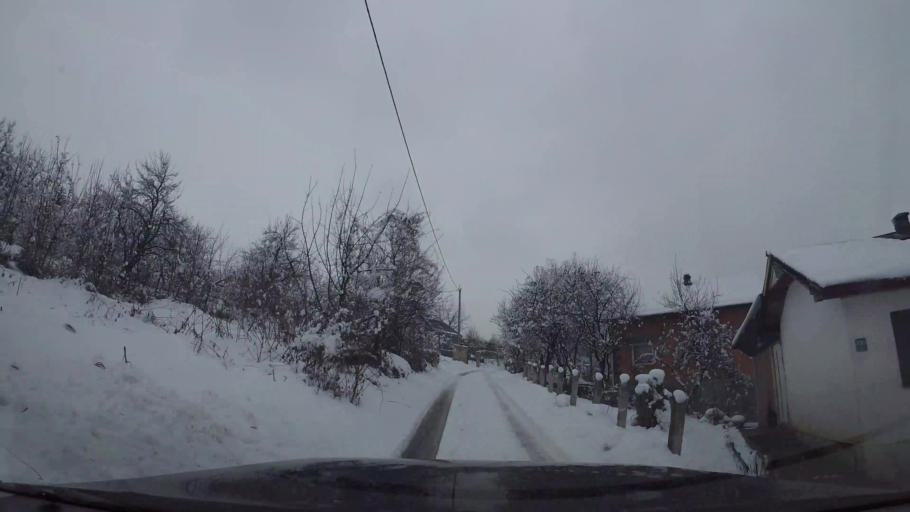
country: BA
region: Federation of Bosnia and Herzegovina
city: Hadzici
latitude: 43.8532
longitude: 18.2571
